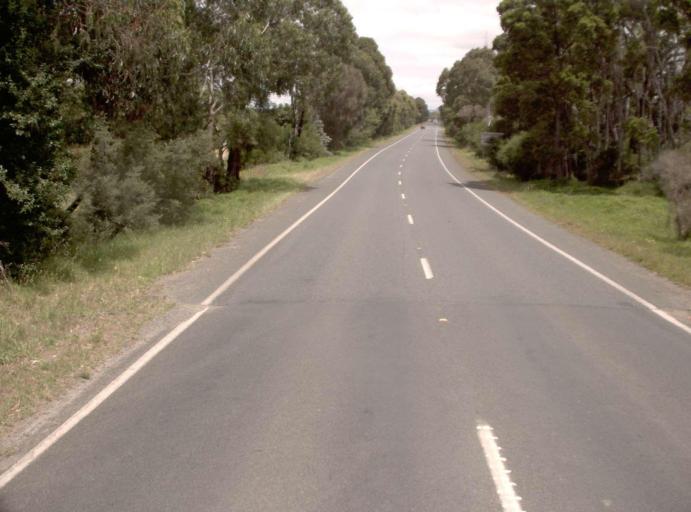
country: AU
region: Victoria
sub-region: Latrobe
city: Traralgon
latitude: -38.5469
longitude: 146.6965
